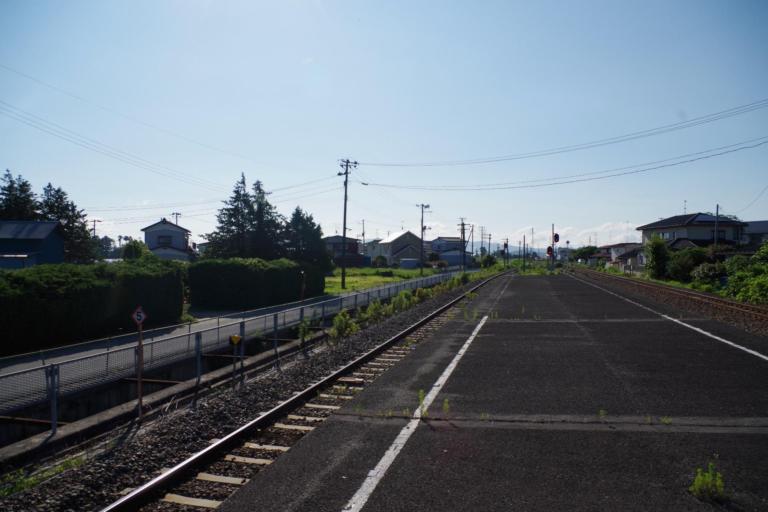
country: JP
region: Miyagi
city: Wakuya
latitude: 38.5119
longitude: 141.1952
